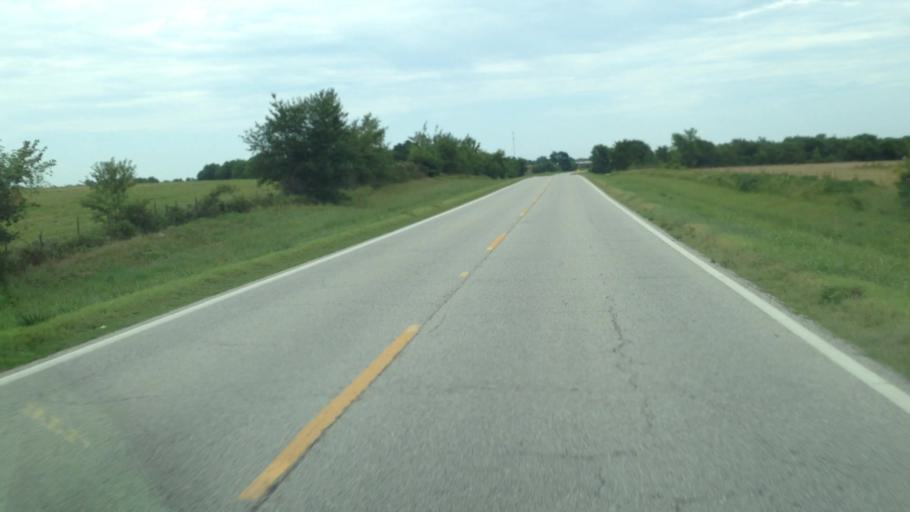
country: US
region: Kansas
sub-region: Labette County
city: Chetopa
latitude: 36.8575
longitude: -95.1156
